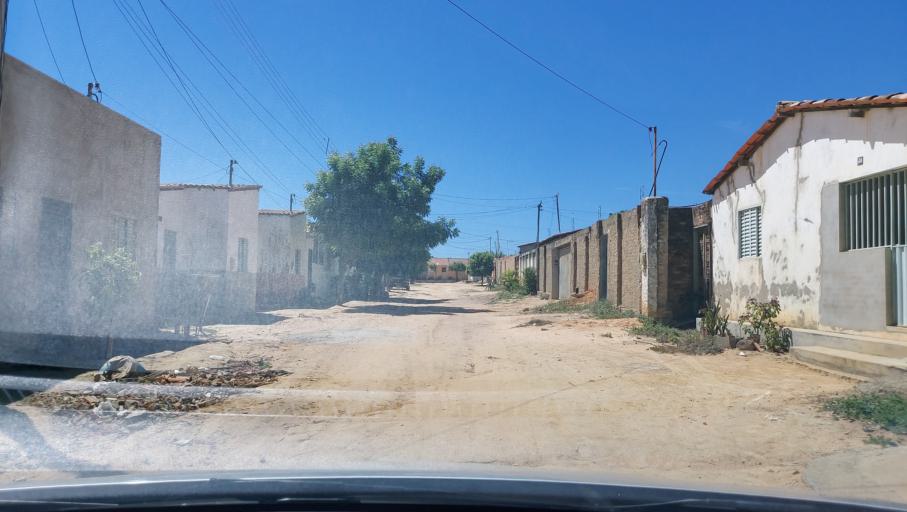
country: BR
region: Bahia
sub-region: Oliveira Dos Brejinhos
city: Beira Rio
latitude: -11.9990
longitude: -42.6317
